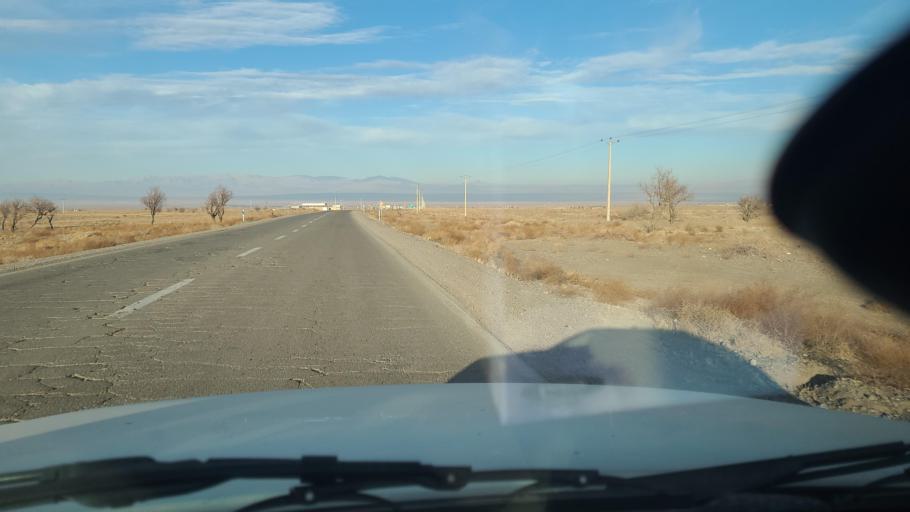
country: IR
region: Razavi Khorasan
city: Neqab
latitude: 36.5025
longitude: 57.5322
